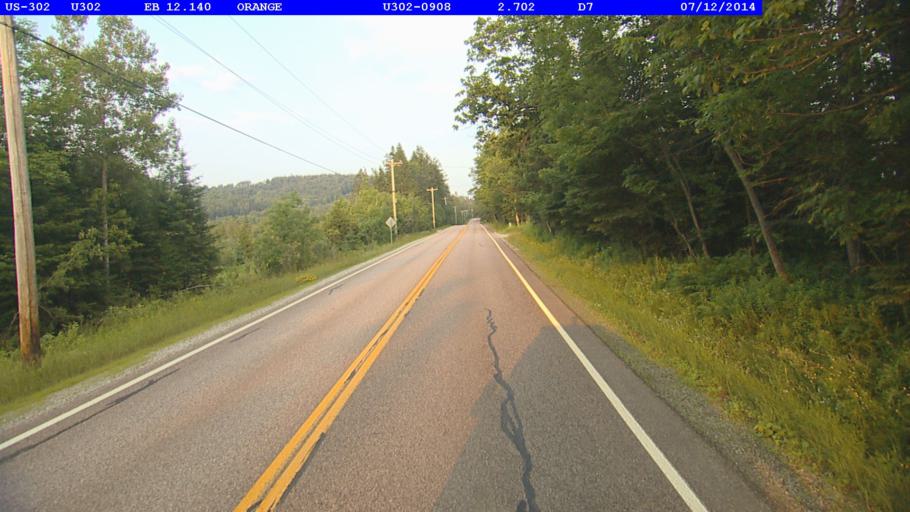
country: US
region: Vermont
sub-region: Washington County
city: South Barre
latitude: 44.1468
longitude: -72.3856
